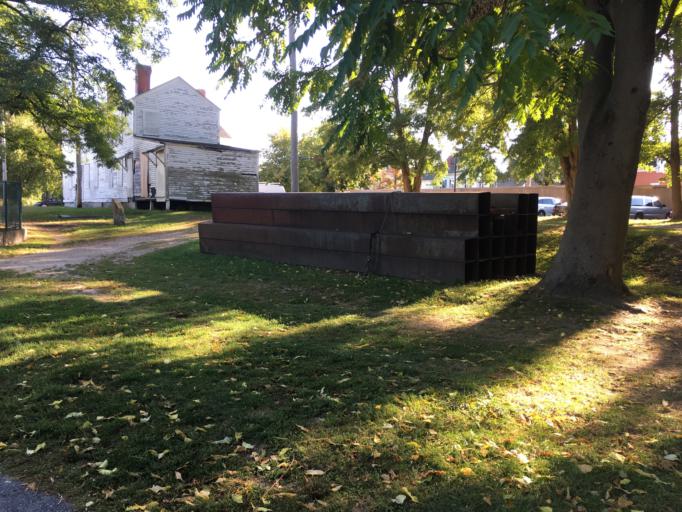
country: US
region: Massachusetts
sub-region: Middlesex County
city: Lowell
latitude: 42.6435
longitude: -71.3296
